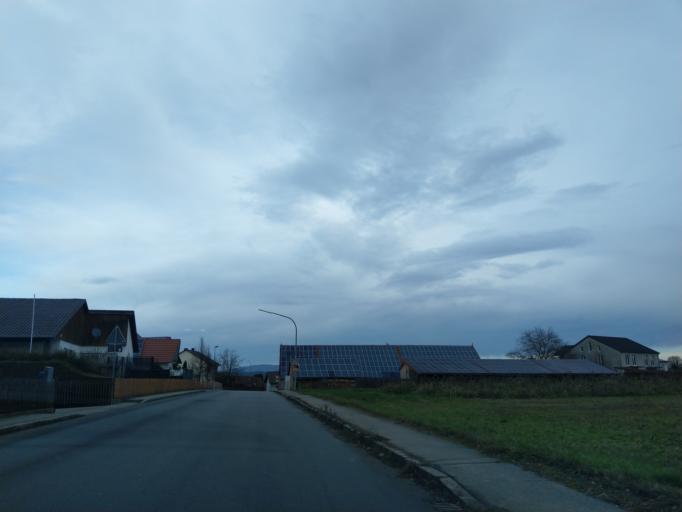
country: DE
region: Bavaria
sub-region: Lower Bavaria
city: Kunzing
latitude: 48.6663
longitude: 13.0717
